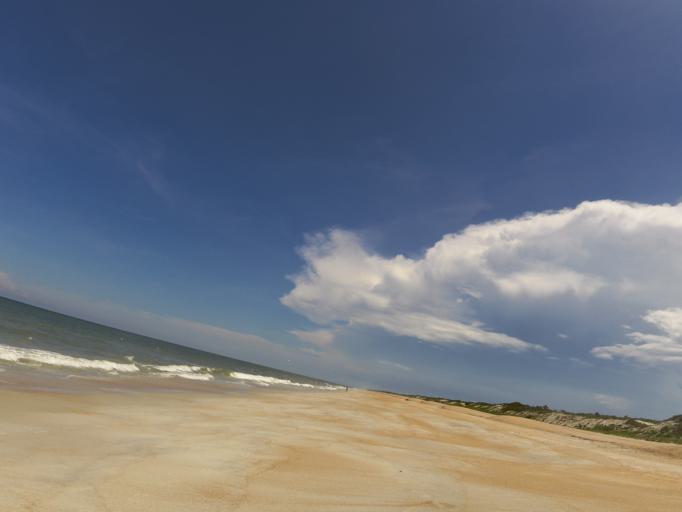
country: US
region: Florida
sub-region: Saint Johns County
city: Palm Valley
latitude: 30.1127
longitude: -81.3434
